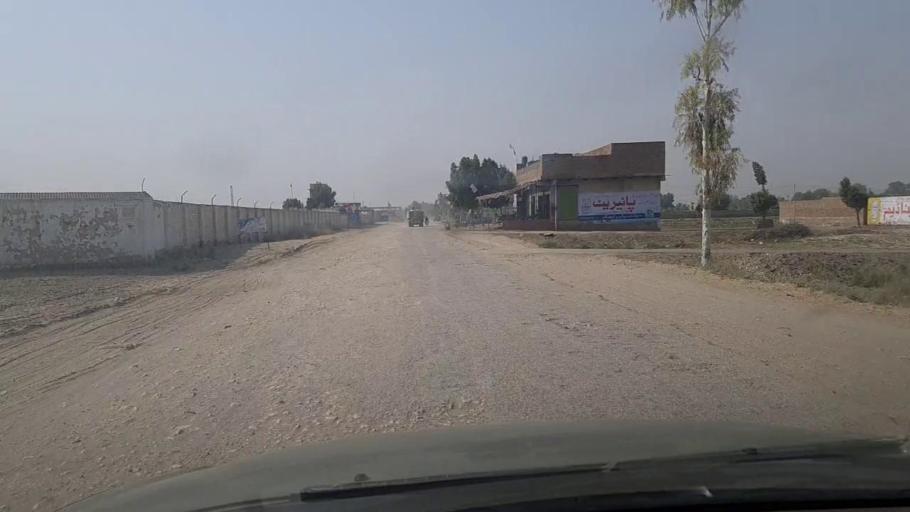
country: PK
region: Sindh
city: Mirpur Mathelo
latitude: 28.0105
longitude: 69.5473
